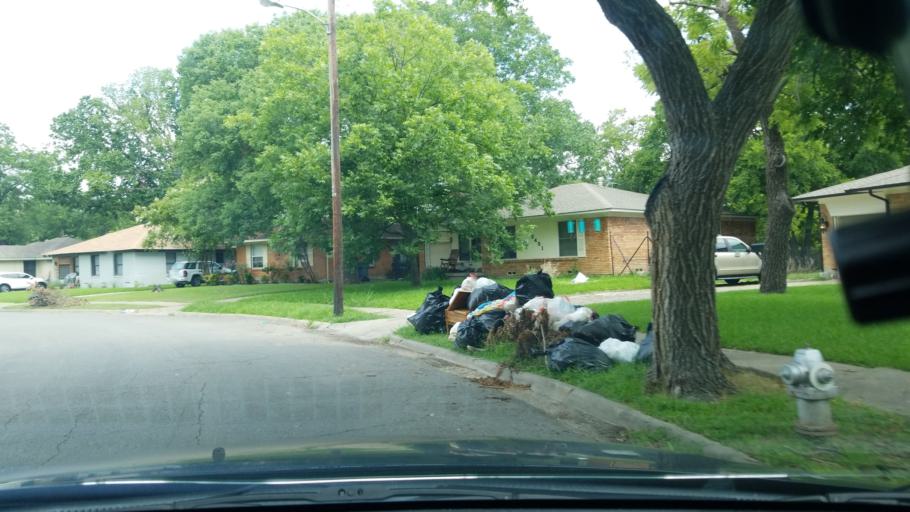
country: US
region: Texas
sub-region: Dallas County
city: Garland
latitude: 32.8293
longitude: -96.6733
